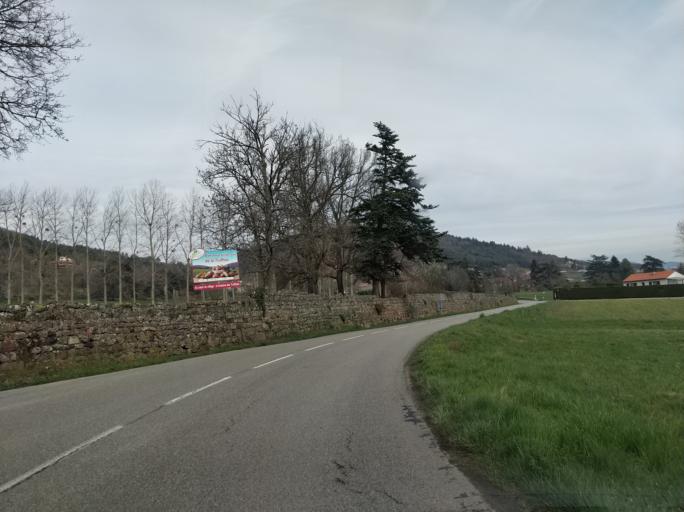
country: FR
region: Rhone-Alpes
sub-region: Departement de l'Ardeche
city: Satillieu
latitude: 45.1831
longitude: 4.6370
